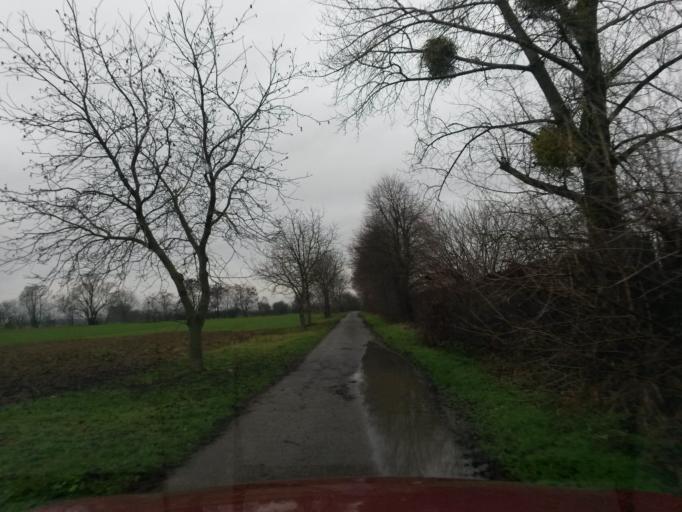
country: SK
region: Kosicky
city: Sobrance
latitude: 48.6354
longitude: 22.0987
